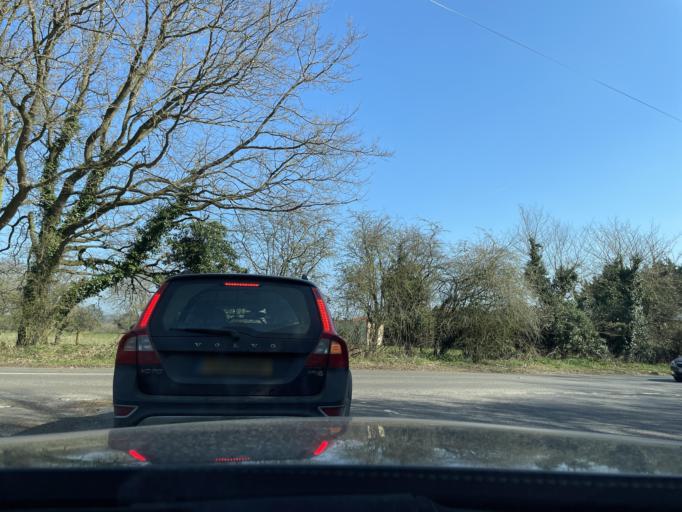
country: GB
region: England
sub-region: Norfolk
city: Hingham
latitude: 52.6169
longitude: 1.0058
